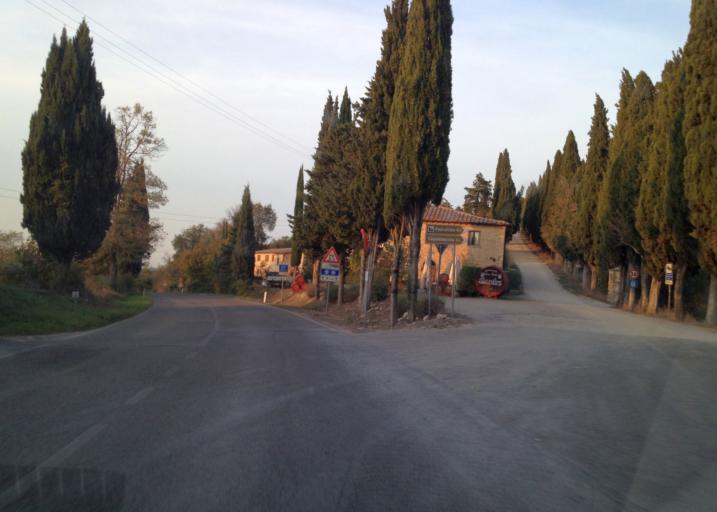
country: IT
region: Tuscany
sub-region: Provincia di Siena
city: Castellina in Chianti
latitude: 43.4908
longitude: 11.3003
